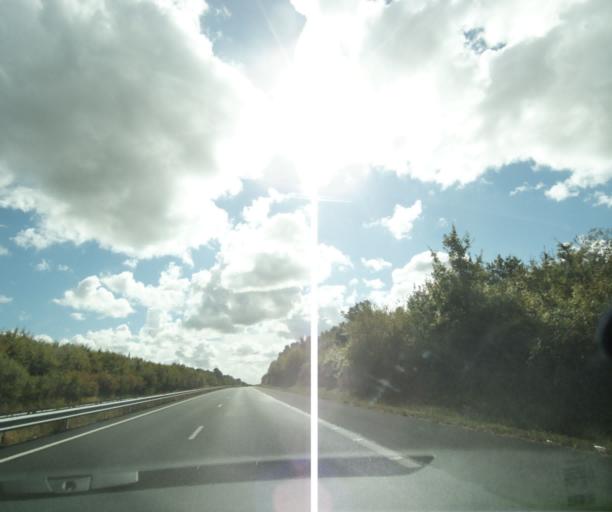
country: FR
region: Poitou-Charentes
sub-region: Departement de la Charente-Maritime
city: Bords
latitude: 45.9027
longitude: -0.7639
